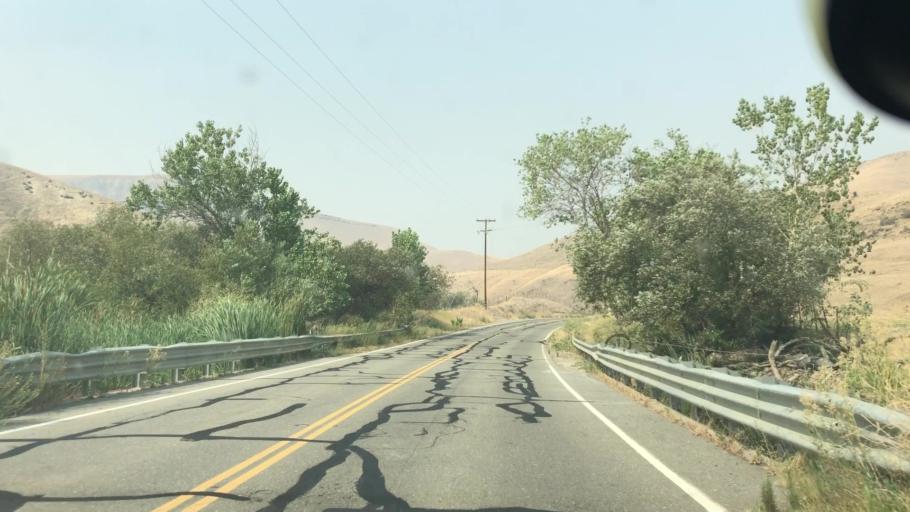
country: US
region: California
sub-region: San Joaquin County
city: Tracy
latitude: 37.6510
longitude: -121.4890
